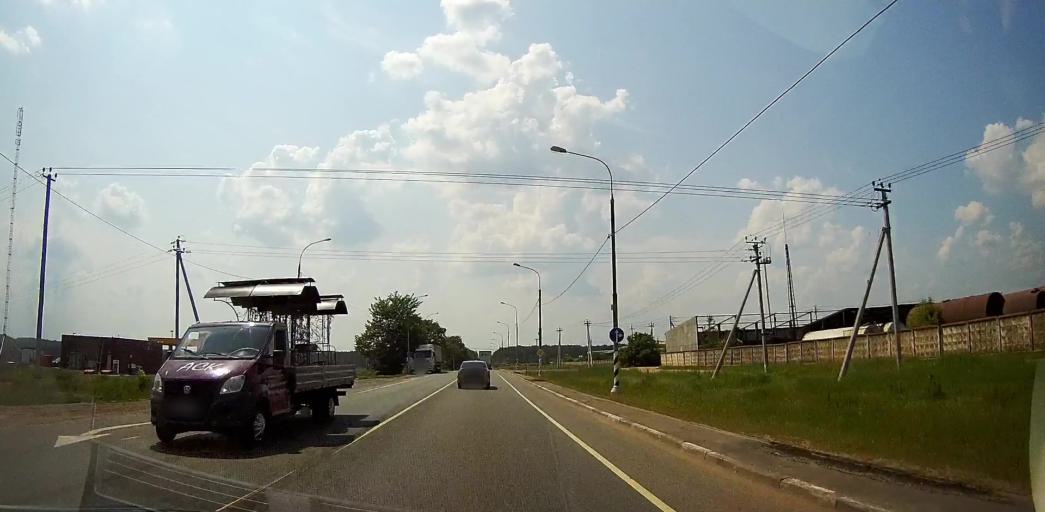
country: RU
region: Moskovskaya
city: Meshcherino
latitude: 55.1444
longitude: 38.2875
